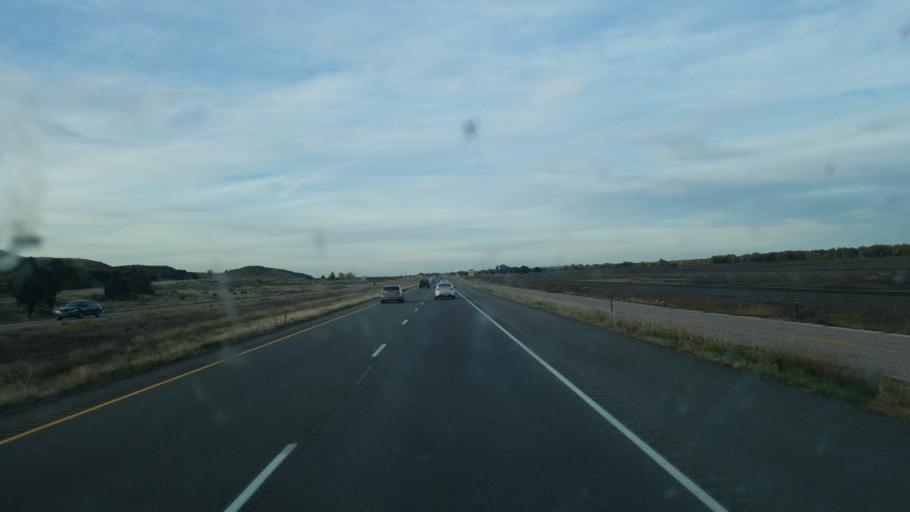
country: US
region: Colorado
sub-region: Pueblo County
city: Pueblo West
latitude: 38.4382
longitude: -104.6062
